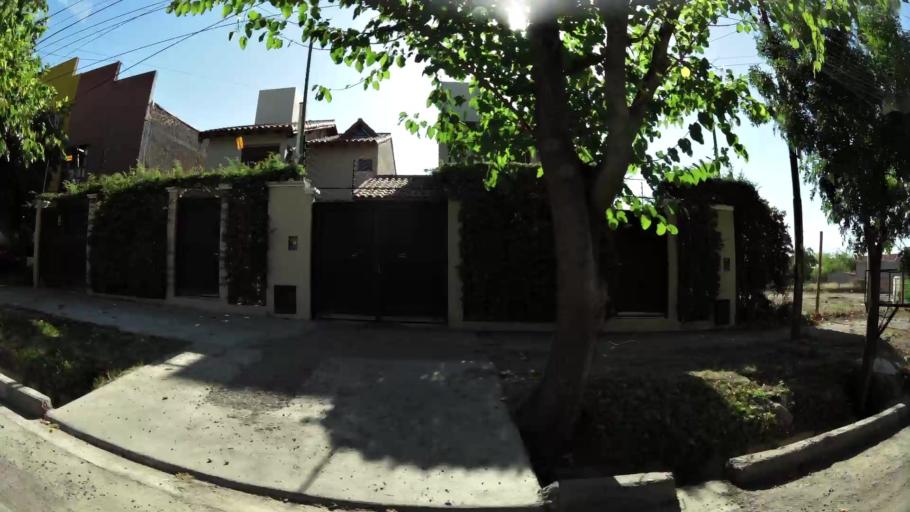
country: AR
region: Mendoza
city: Mendoza
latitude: -32.9041
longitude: -68.8180
